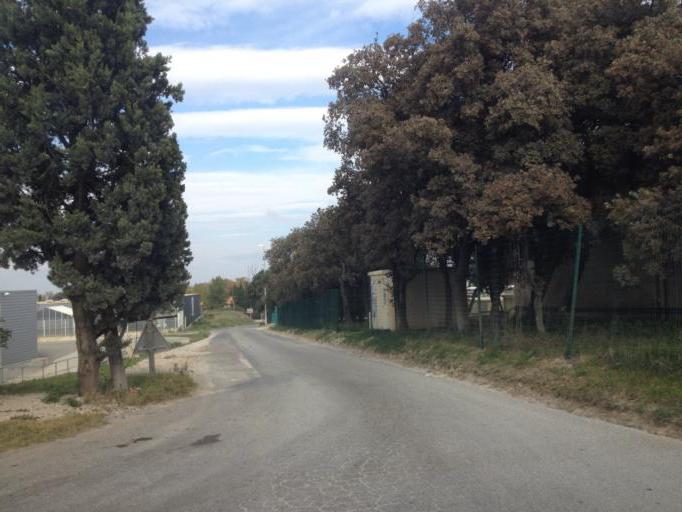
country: FR
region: Provence-Alpes-Cote d'Azur
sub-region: Departement du Vaucluse
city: Orange
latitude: 44.1186
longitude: 4.8442
